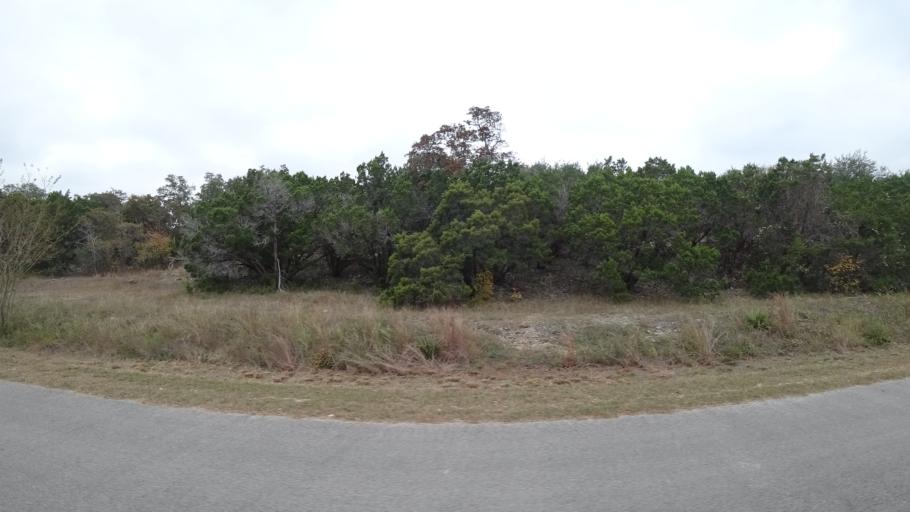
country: US
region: Texas
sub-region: Williamson County
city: Anderson Mill
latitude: 30.4480
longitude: -97.8396
